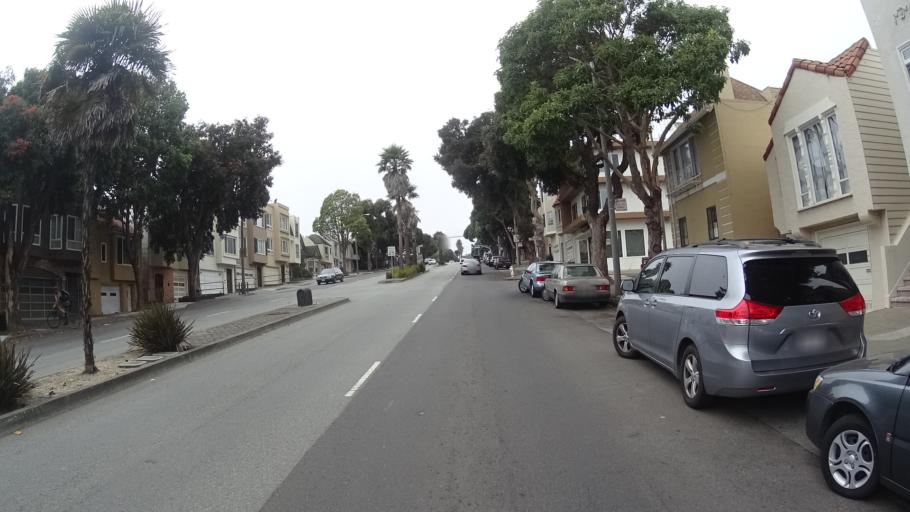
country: US
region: California
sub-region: San Mateo County
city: Daly City
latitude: 37.7316
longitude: -122.4469
